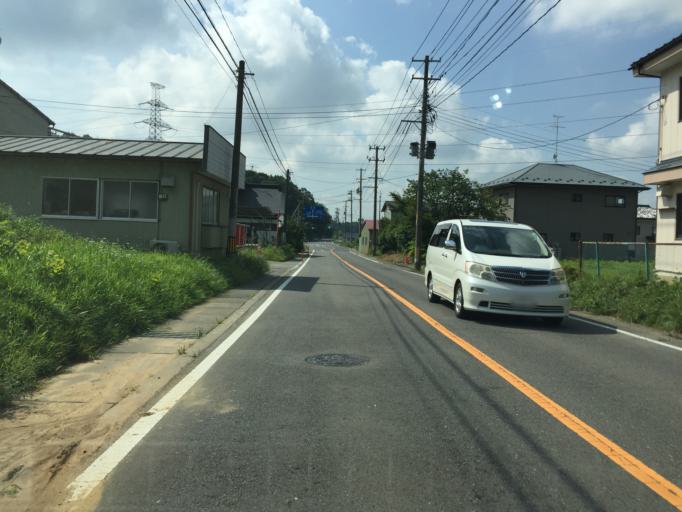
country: JP
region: Fukushima
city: Motomiya
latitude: 37.5409
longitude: 140.4039
